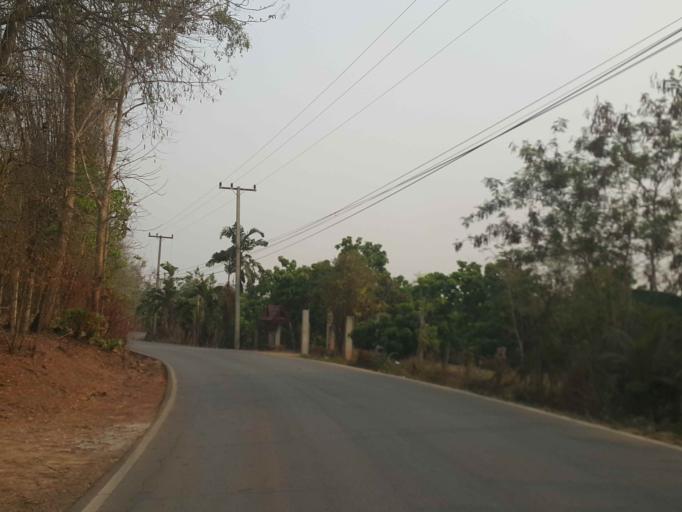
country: TH
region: Chiang Mai
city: Mae Taeng
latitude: 19.0986
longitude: 98.9002
